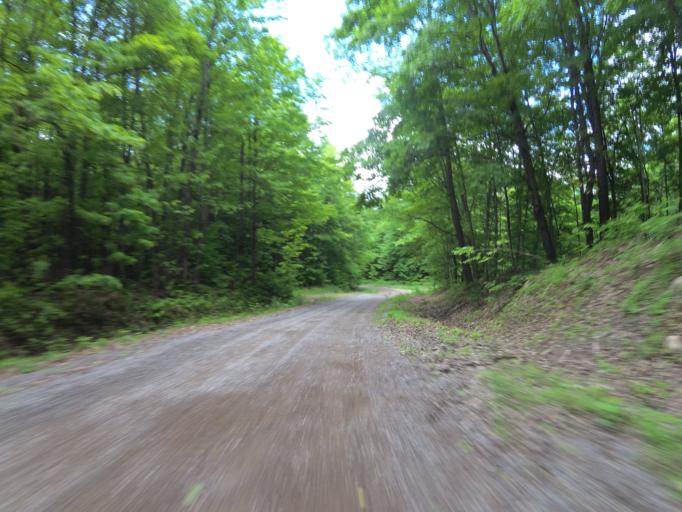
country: CA
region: Ontario
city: Renfrew
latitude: 45.1360
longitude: -76.8796
